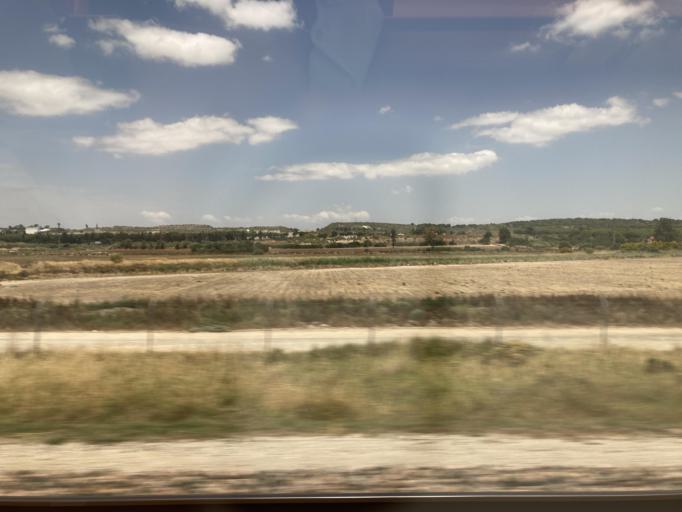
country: ES
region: Andalusia
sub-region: Provincia de Cadiz
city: El Puerto de Santa Maria
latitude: 36.6177
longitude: -6.1836
